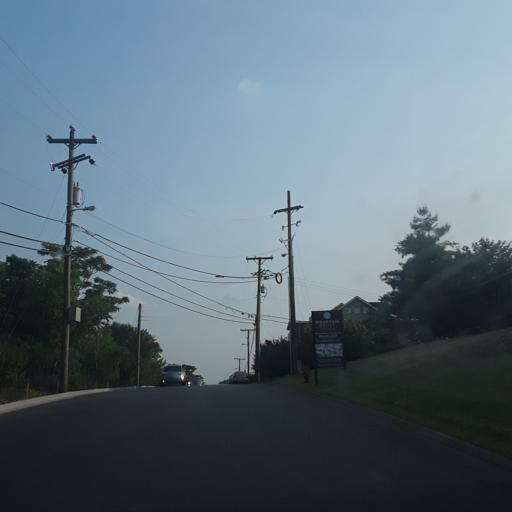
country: US
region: Tennessee
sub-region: Williamson County
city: Brentwood Estates
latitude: 36.0427
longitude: -86.7202
